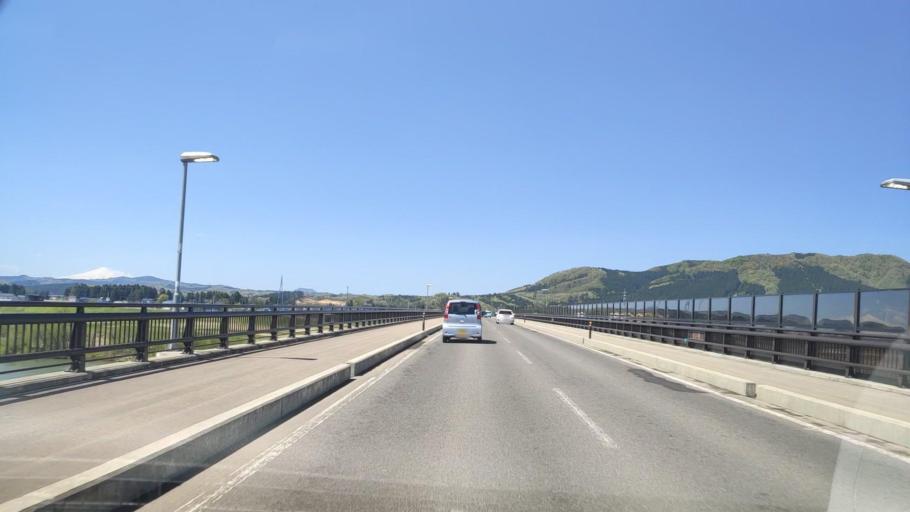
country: JP
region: Akita
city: Omagari
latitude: 39.4506
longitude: 140.4689
